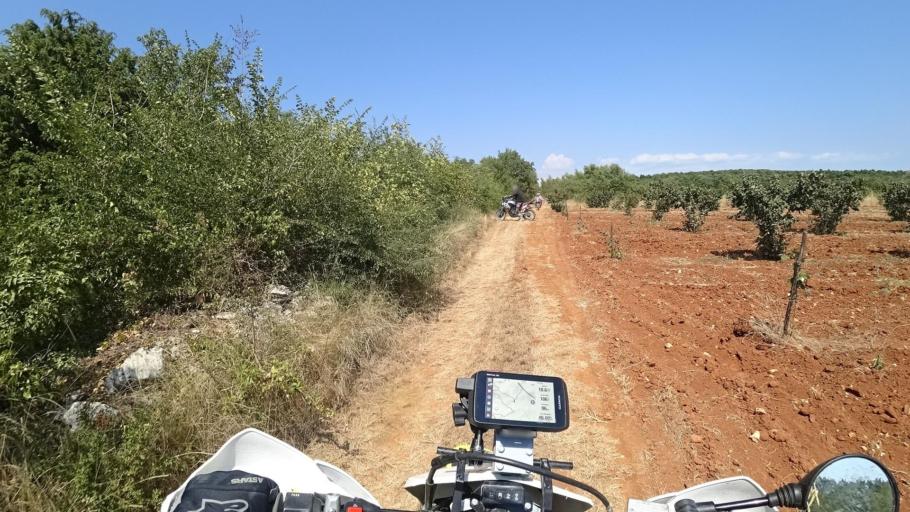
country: HR
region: Istarska
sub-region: Grad Rovinj
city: Rovinj
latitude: 45.1408
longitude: 13.7467
